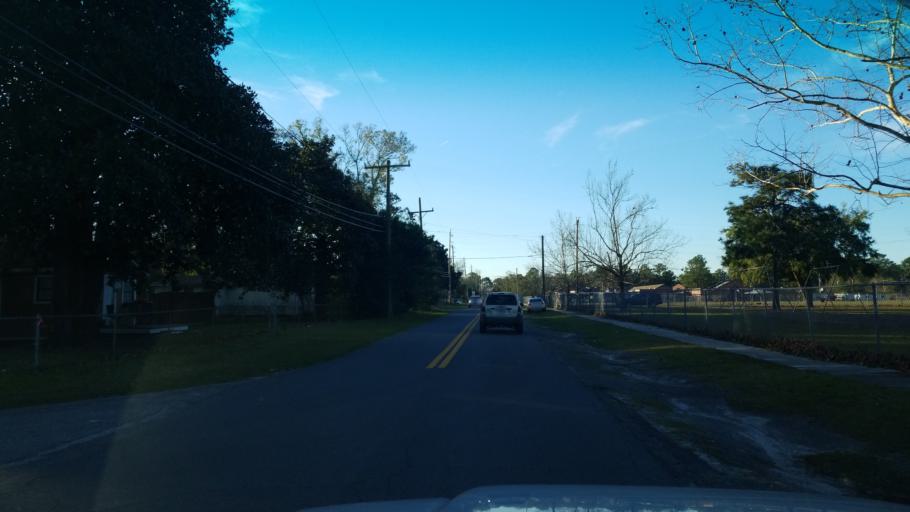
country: US
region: Florida
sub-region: Duval County
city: Jacksonville
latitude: 30.3276
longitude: -81.7860
